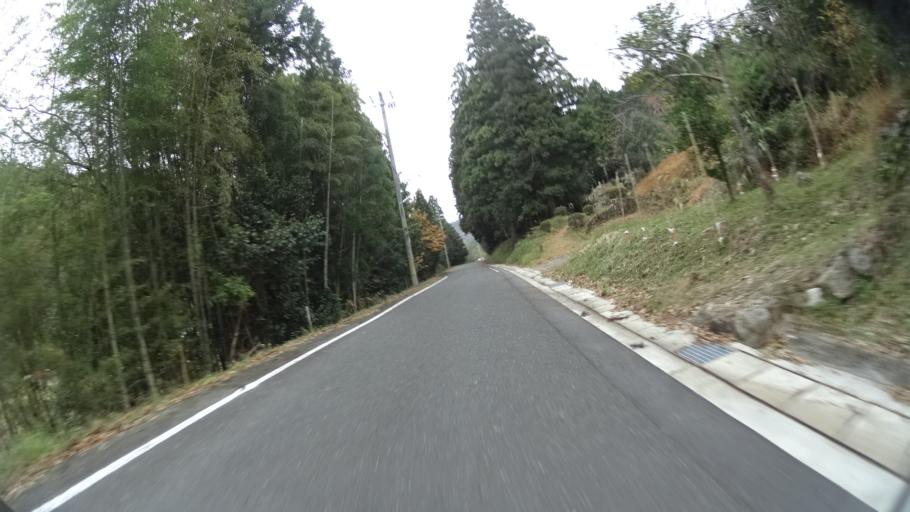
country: JP
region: Hyogo
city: Sasayama
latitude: 35.1605
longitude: 135.3064
